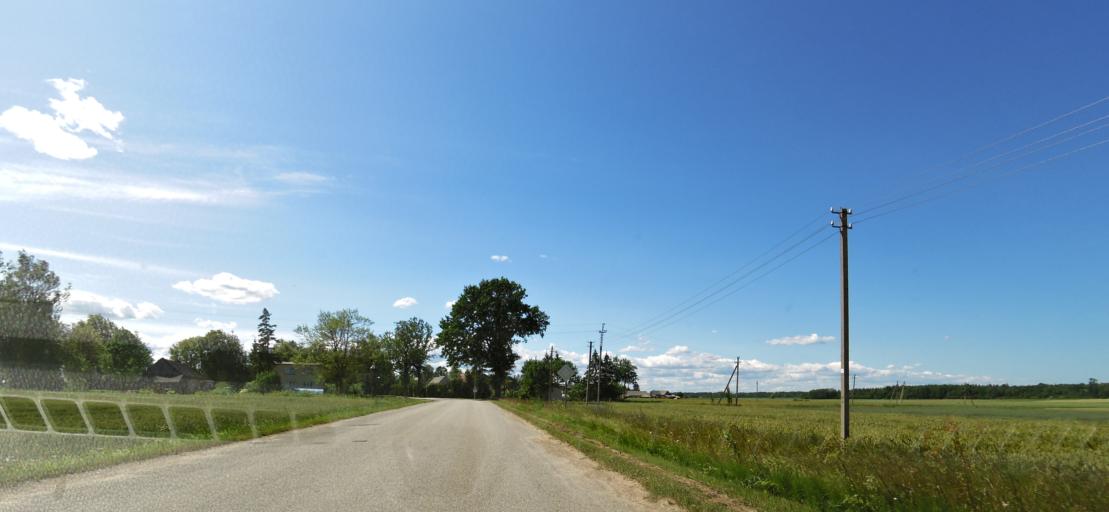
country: LV
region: Bauskas Rajons
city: Bauska
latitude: 56.2531
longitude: 24.3110
